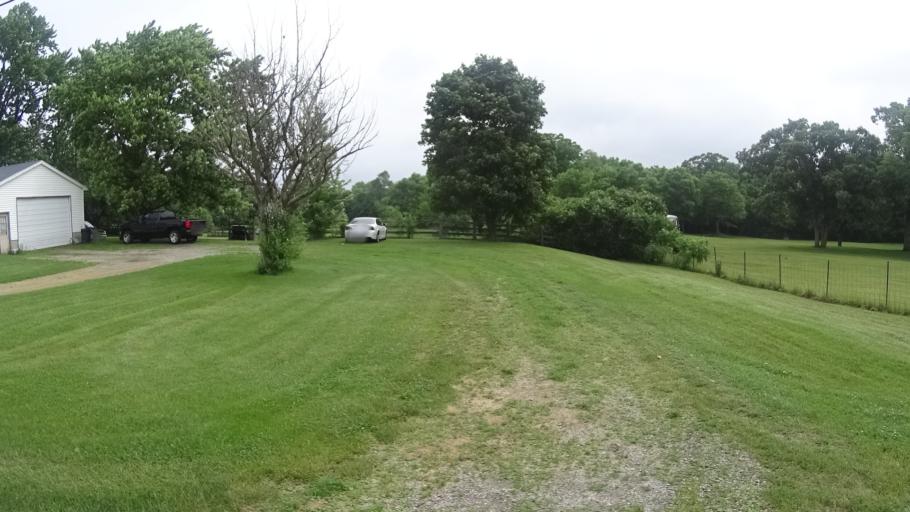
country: US
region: Ohio
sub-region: Erie County
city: Sandusky
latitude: 41.3592
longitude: -82.7579
